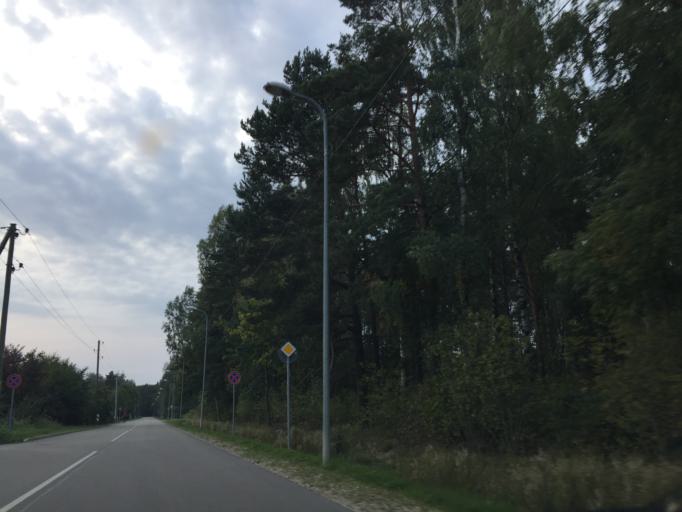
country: LV
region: Saulkrastu
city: Saulkrasti
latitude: 57.3220
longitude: 24.4228
